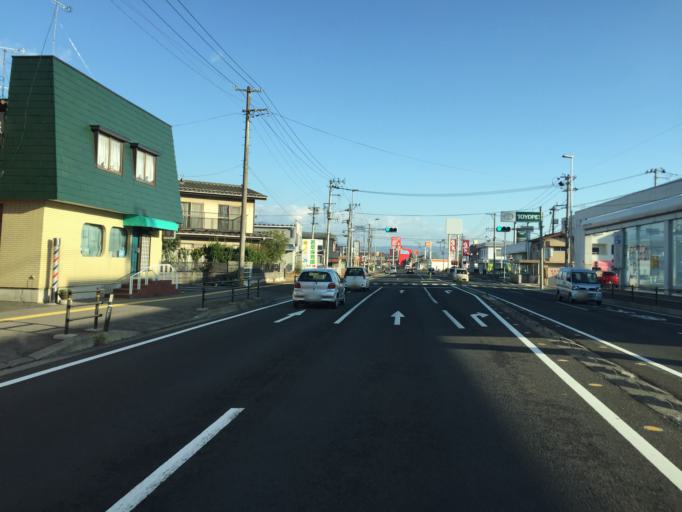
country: JP
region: Fukushima
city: Fukushima-shi
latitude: 37.7818
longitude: 140.4865
